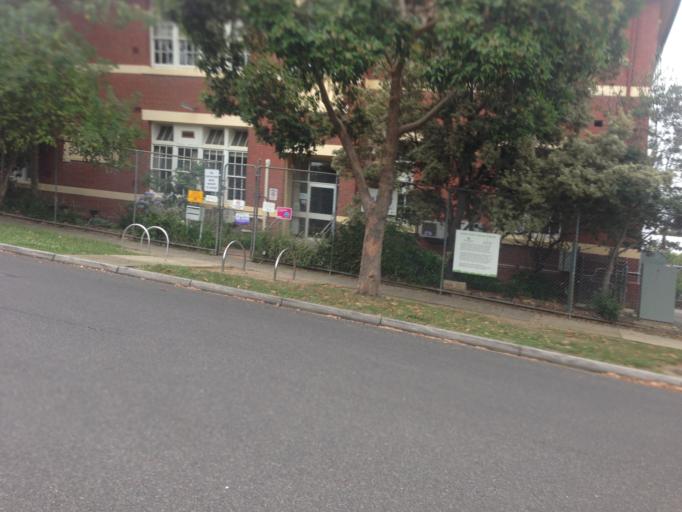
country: AU
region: Victoria
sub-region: Darebin
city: Thornbury
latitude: -37.7622
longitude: 145.0079
